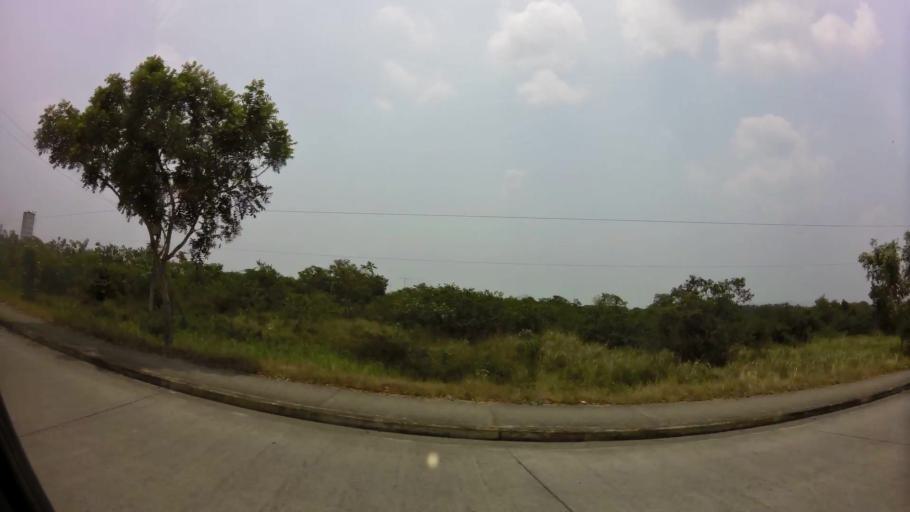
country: HN
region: Cortes
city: La Lima
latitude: 15.4507
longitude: -87.9358
